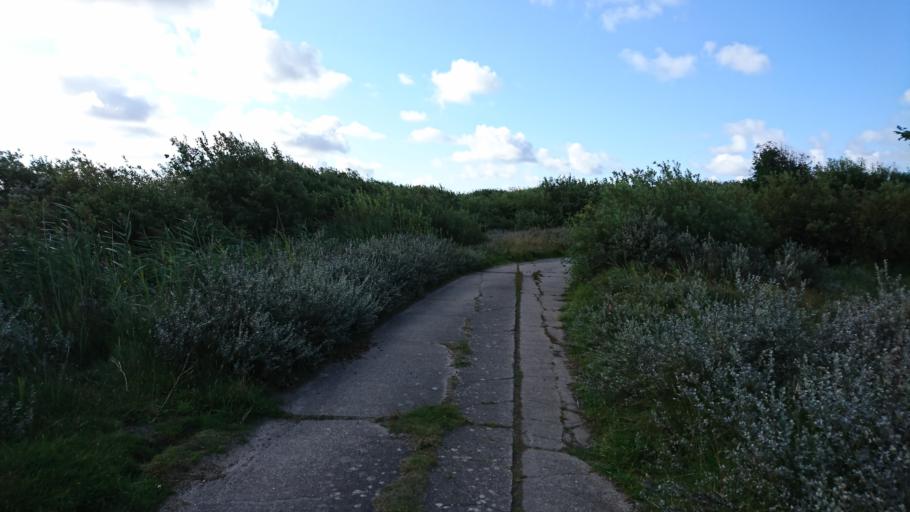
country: DK
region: South Denmark
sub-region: Fano Kommune
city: Nordby
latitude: 55.4457
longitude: 8.3614
